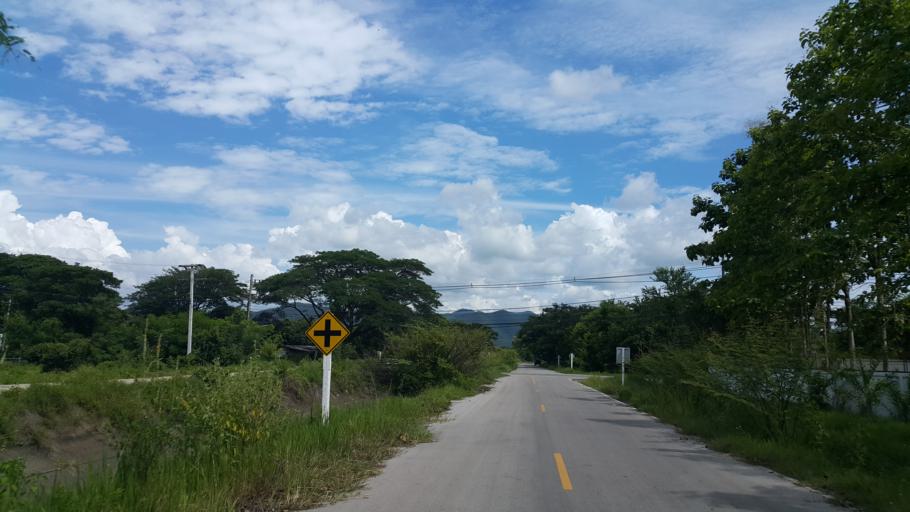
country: TH
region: Chiang Mai
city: Mae On
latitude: 18.7440
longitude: 99.2006
